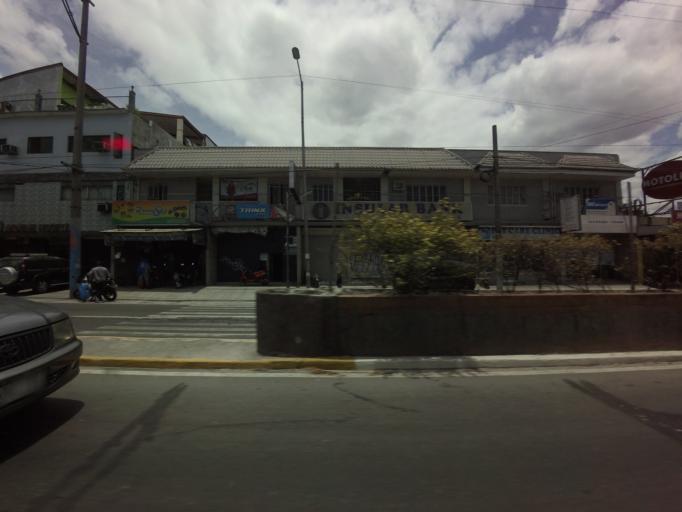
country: PH
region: Metro Manila
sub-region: Marikina
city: Calumpang
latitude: 14.6124
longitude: 121.1030
